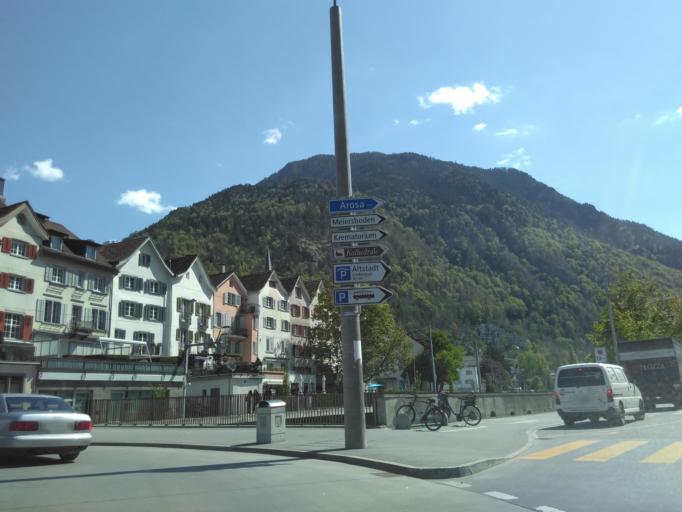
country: CH
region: Grisons
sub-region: Plessur District
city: Chur
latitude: 46.8477
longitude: 9.5294
